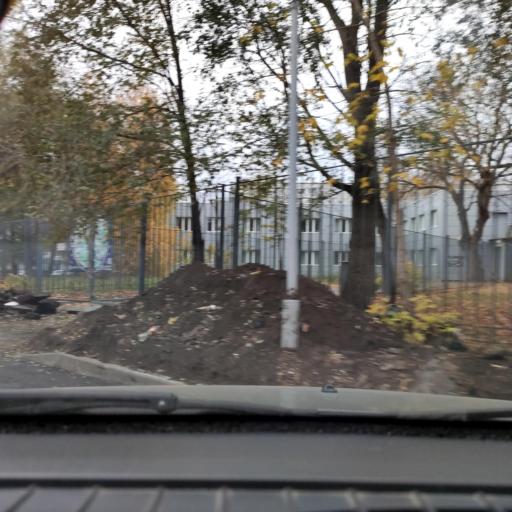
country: RU
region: Samara
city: Tol'yatti
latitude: 53.5176
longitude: 49.2627
